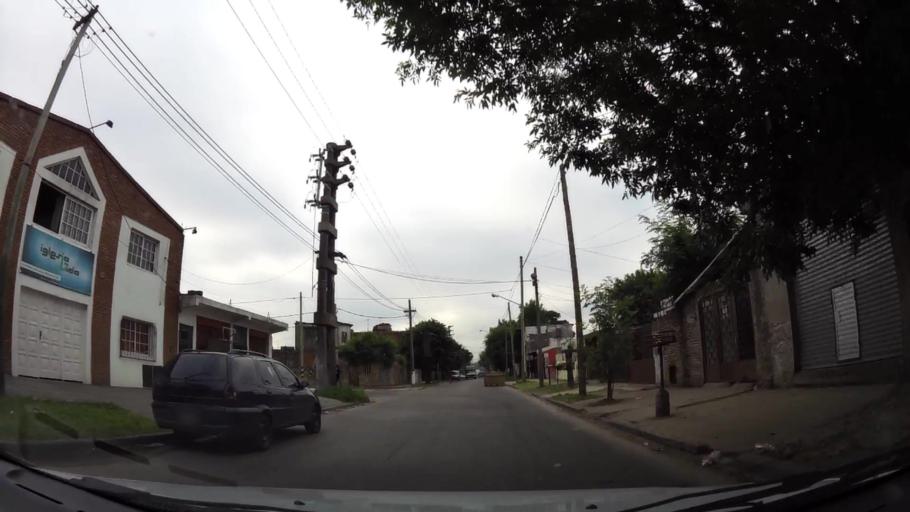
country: AR
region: Buenos Aires
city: San Justo
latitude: -34.6879
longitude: -58.5897
